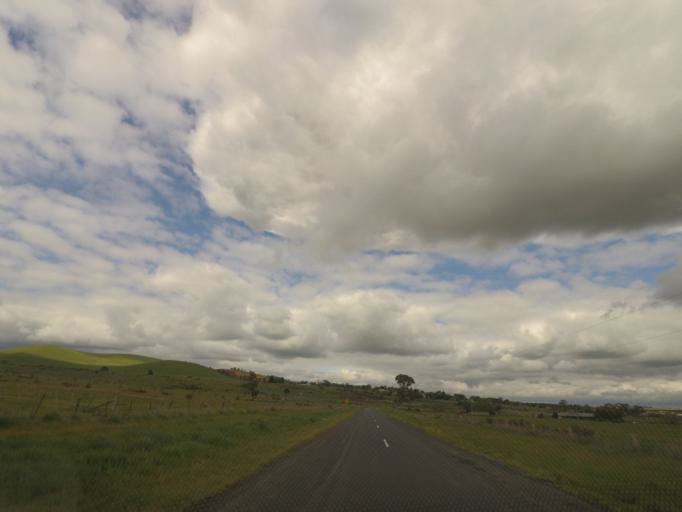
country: AU
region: Victoria
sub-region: Hume
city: Craigieburn
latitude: -37.4681
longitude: 144.9633
